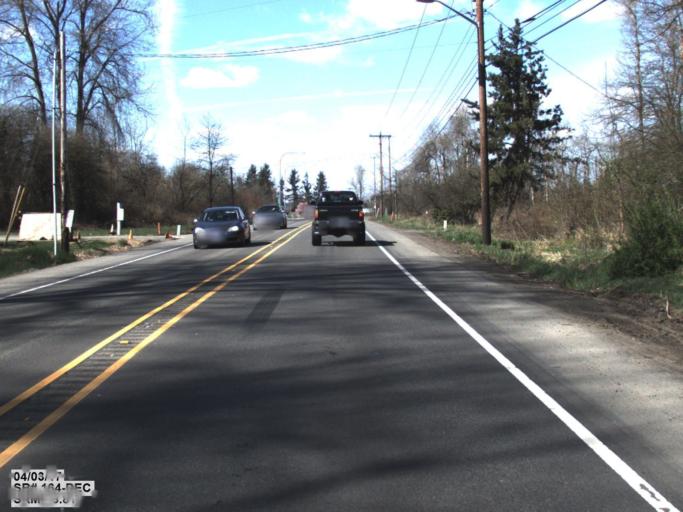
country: US
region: Washington
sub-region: King County
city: Lake Morton-Berrydale
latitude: 47.2517
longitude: -122.1193
